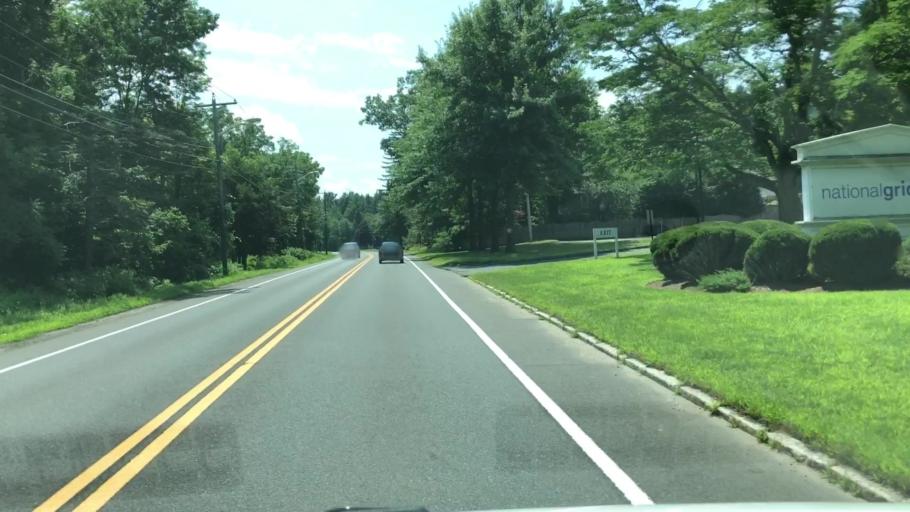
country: US
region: Massachusetts
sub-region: Hampshire County
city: Williamsburg
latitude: 42.3659
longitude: -72.6938
